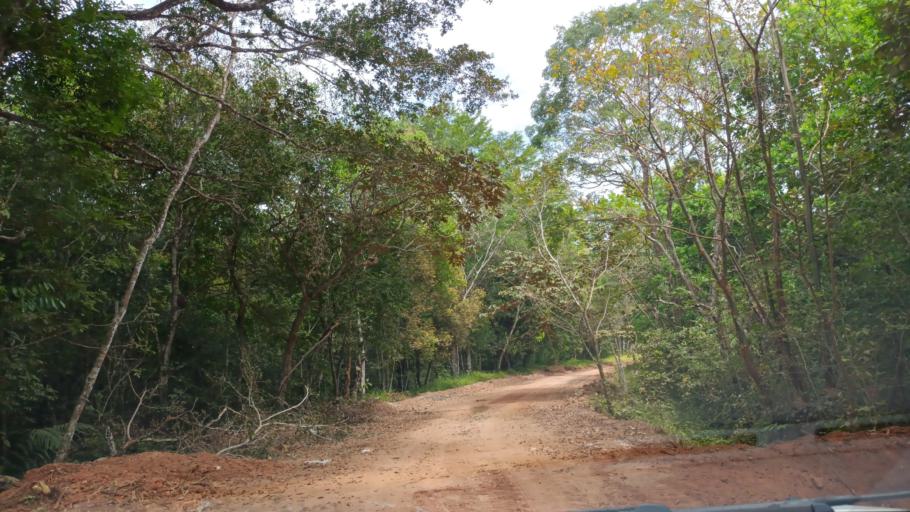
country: PA
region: Panama
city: La Cabima
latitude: 9.1304
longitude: -79.5029
